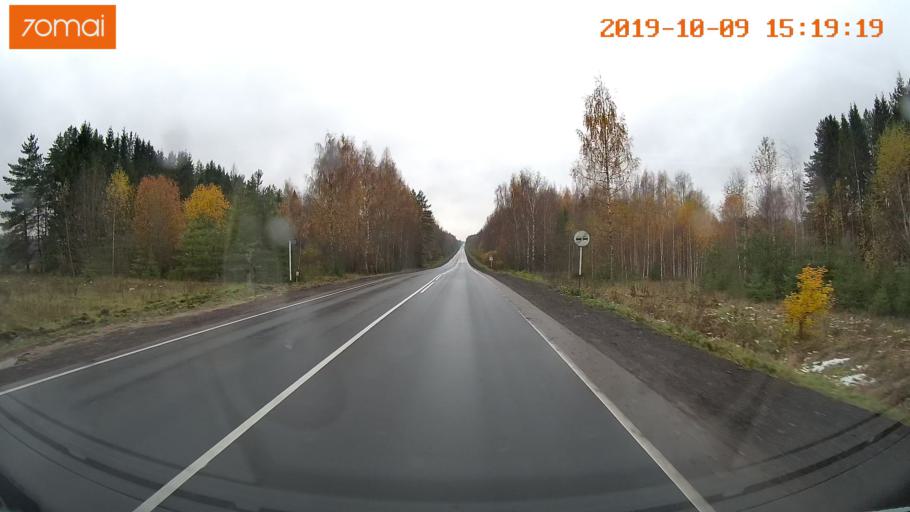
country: RU
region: Kostroma
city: Susanino
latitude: 58.0770
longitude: 41.5585
